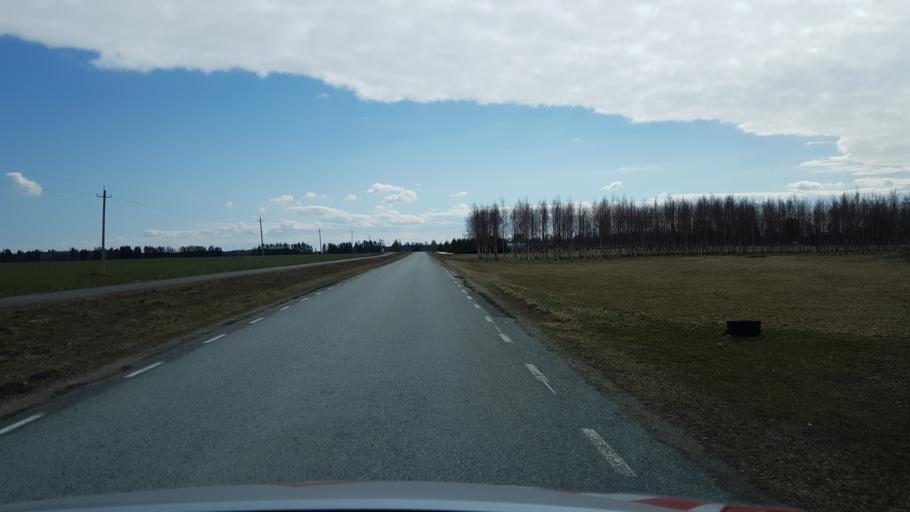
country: EE
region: Laeaene-Virumaa
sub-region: Haljala vald
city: Haljala
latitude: 59.4048
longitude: 26.2617
